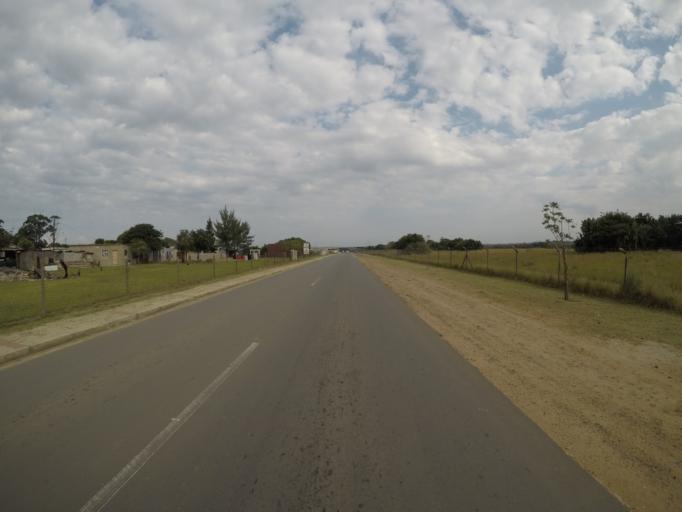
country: ZA
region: KwaZulu-Natal
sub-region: uThungulu District Municipality
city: Richards Bay
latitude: -28.7445
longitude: 32.0908
